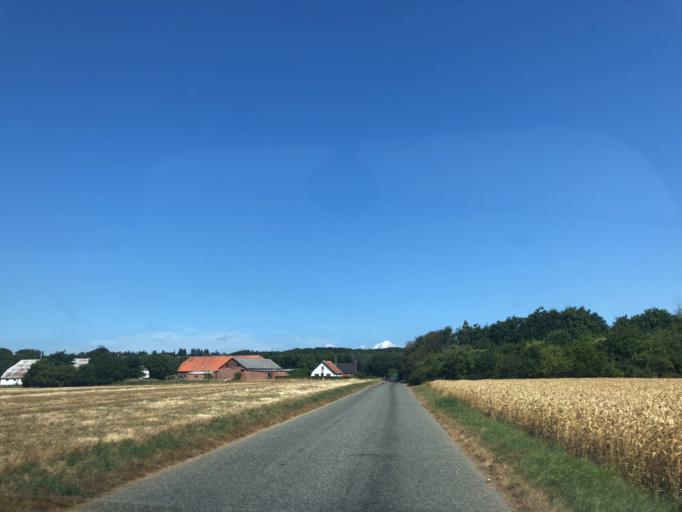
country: DK
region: North Denmark
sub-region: Morso Kommune
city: Nykobing Mors
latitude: 56.8194
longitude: 8.9993
